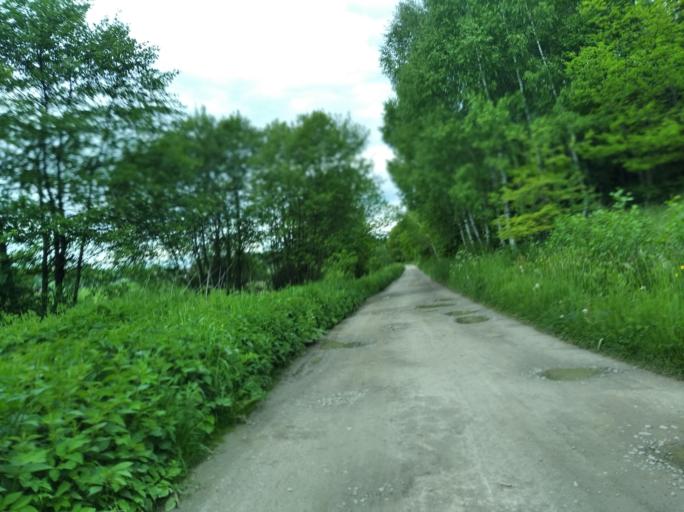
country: PL
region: Subcarpathian Voivodeship
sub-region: Powiat brzozowski
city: Zmiennica
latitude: 49.6719
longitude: 21.9787
